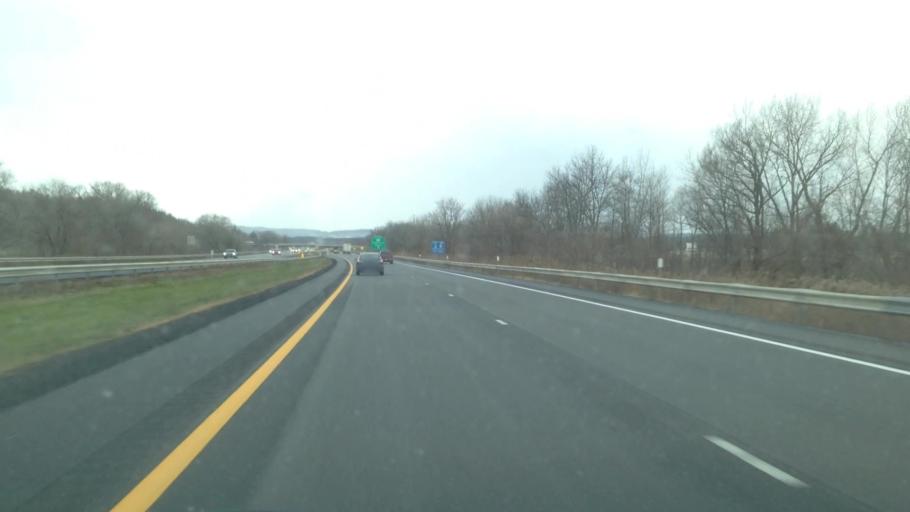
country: US
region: New York
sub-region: Montgomery County
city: Fonda
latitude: 42.9428
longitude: -74.3490
